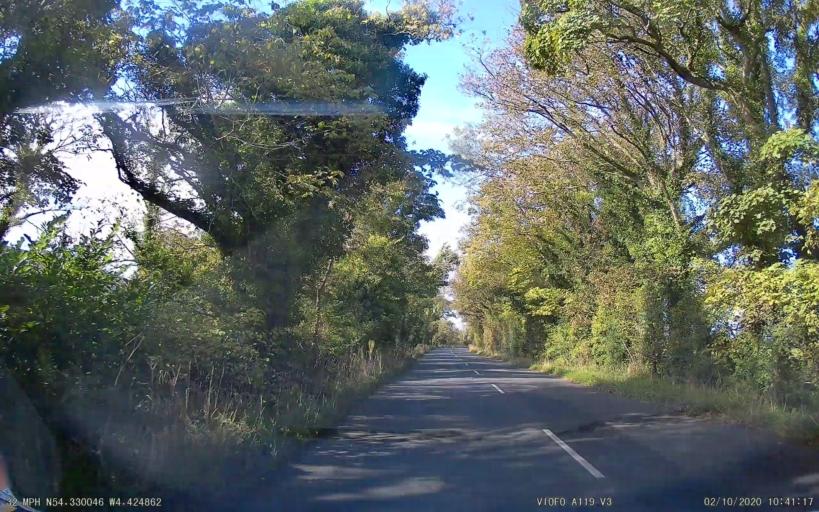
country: IM
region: Ramsey
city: Ramsey
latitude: 54.3300
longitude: -4.4249
